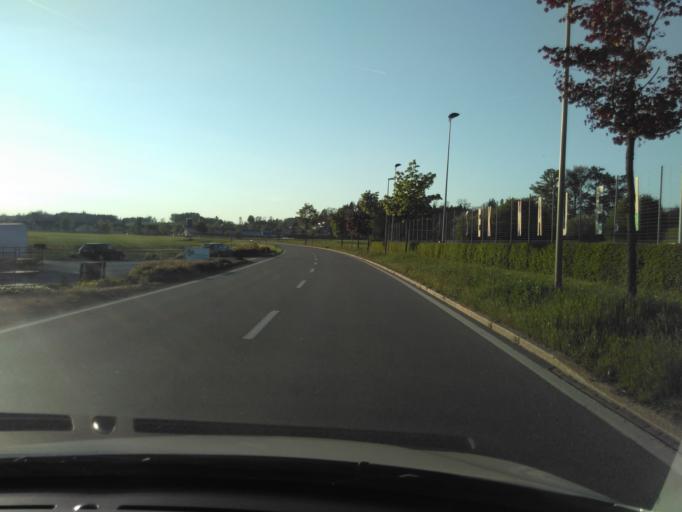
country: CH
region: Zurich
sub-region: Bezirk Hinwil
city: Tann
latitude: 47.2716
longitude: 8.8516
